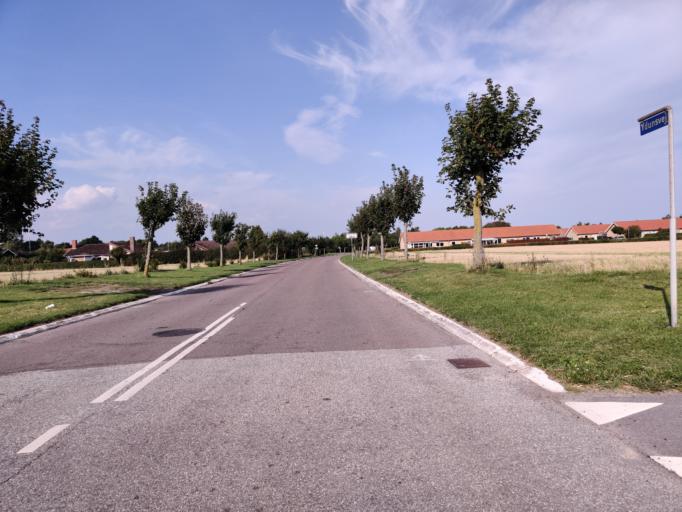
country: DK
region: Zealand
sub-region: Guldborgsund Kommune
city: Nykobing Falster
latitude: 54.7038
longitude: 11.9259
